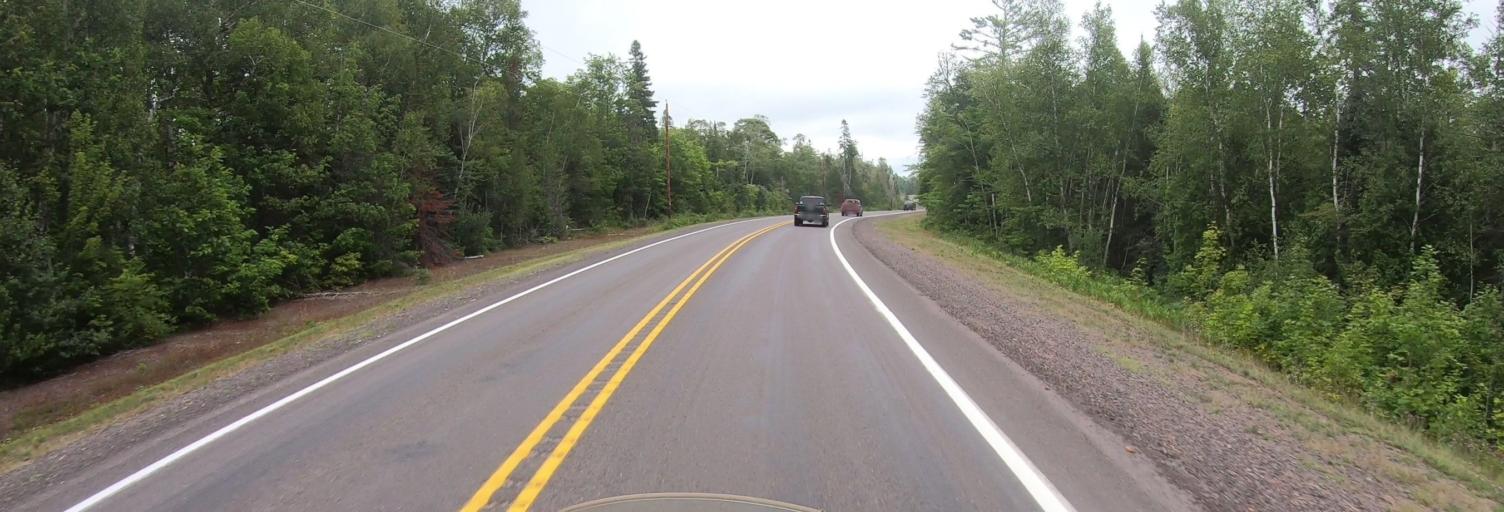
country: US
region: Michigan
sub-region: Keweenaw County
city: Eagle River
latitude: 47.4193
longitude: -88.1299
